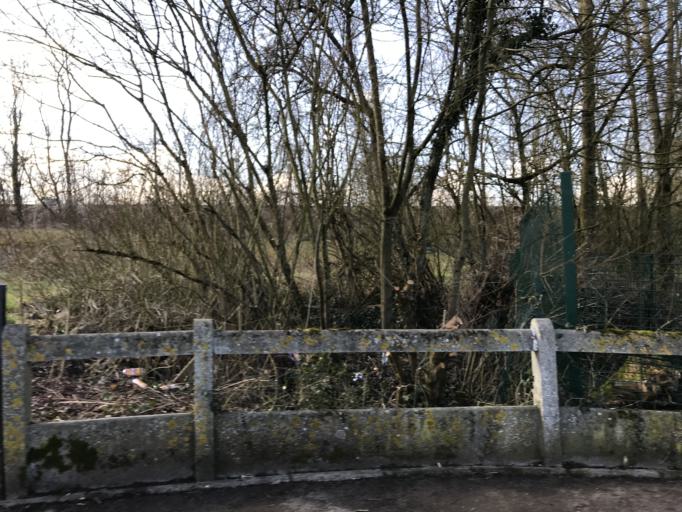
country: FR
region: Nord-Pas-de-Calais
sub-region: Departement du Pas-de-Calais
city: Bully-les-Mines
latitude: 50.4531
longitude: 2.7229
